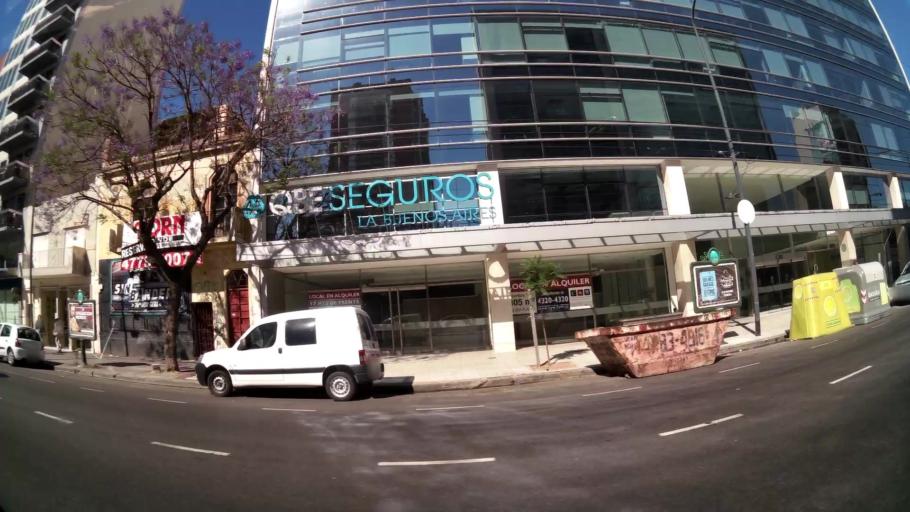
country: AR
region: Buenos Aires F.D.
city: Colegiales
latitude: -34.5537
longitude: -58.4504
